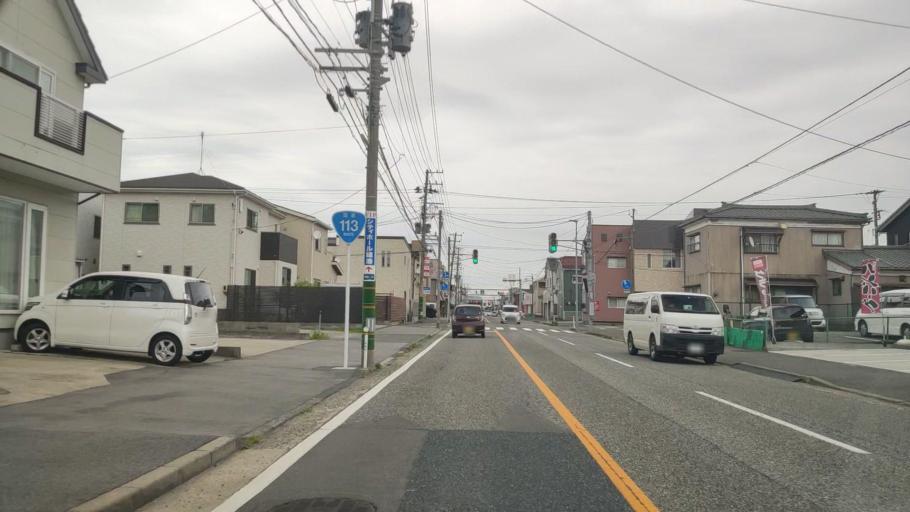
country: JP
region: Niigata
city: Niigata-shi
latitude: 37.9407
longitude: 139.0806
